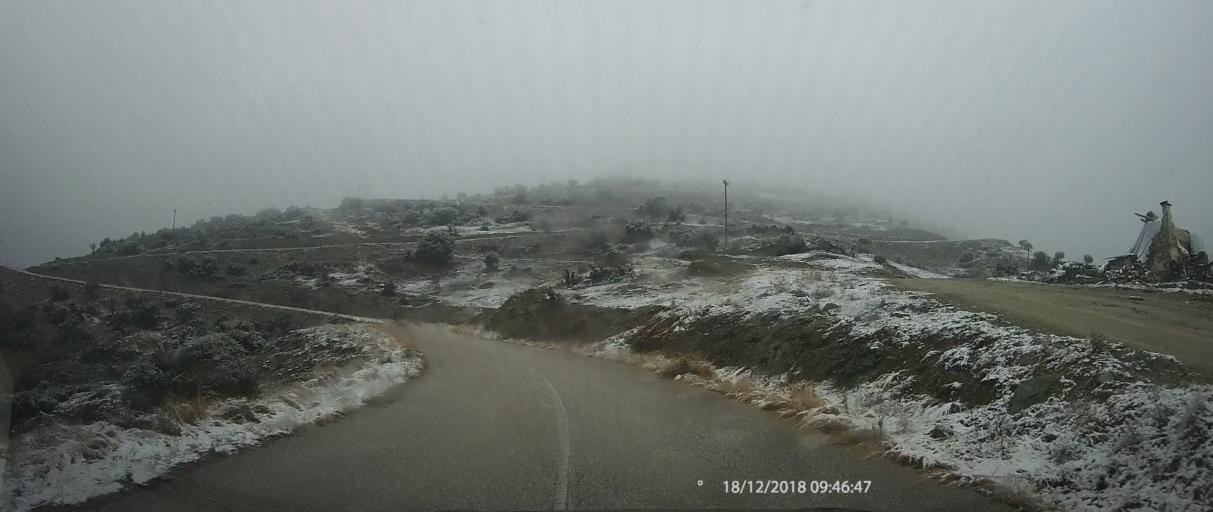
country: GR
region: Thessaly
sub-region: Nomos Larisis
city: Livadi
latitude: 40.0279
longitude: 22.2516
